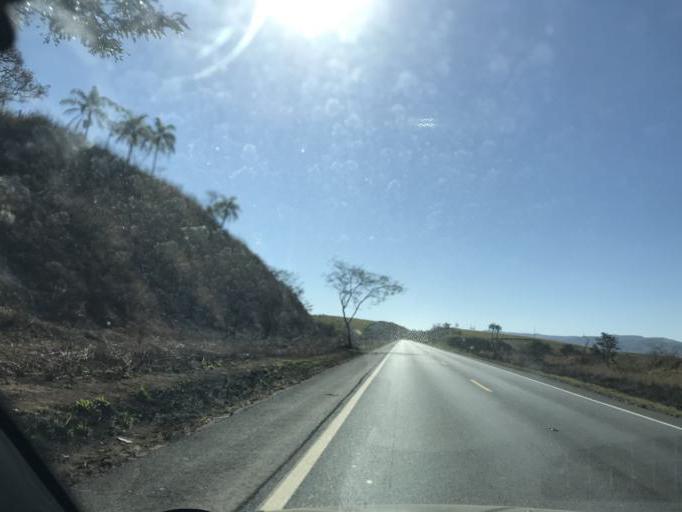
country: BR
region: Minas Gerais
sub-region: Bambui
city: Bambui
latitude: -19.8500
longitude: -45.9970
